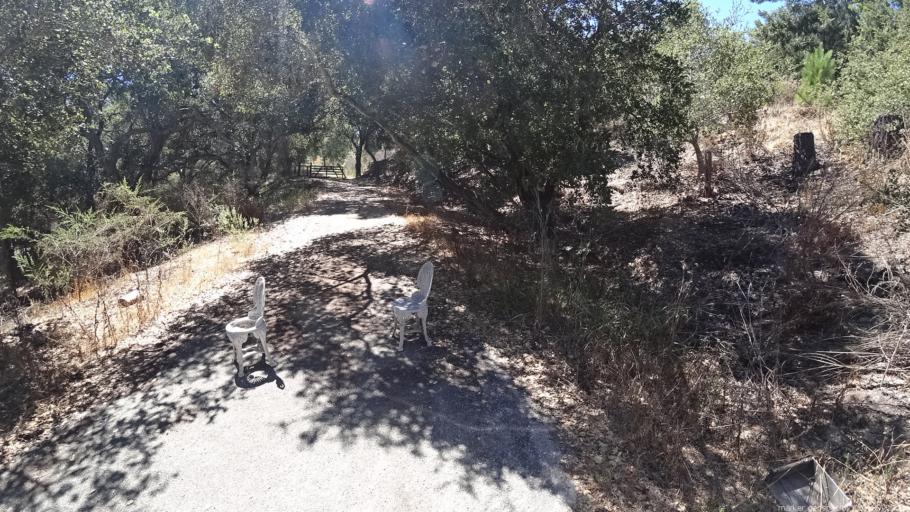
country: US
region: California
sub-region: Monterey County
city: Carmel Valley Village
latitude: 36.5486
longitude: -121.7483
